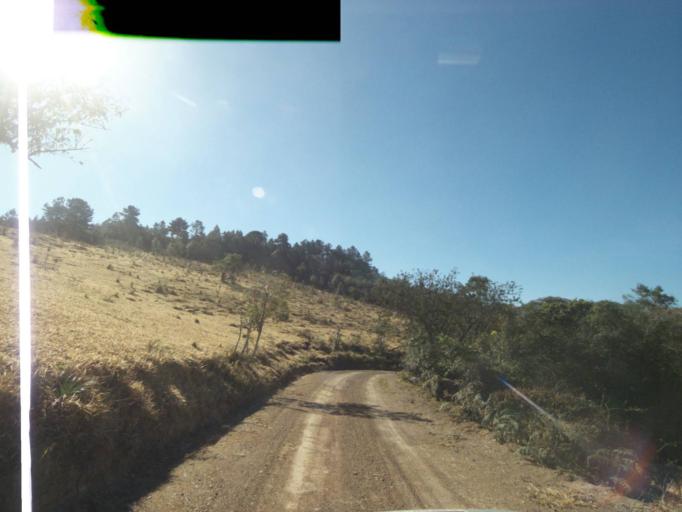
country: BR
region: Parana
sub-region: Tibagi
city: Tibagi
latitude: -24.5799
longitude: -50.4811
